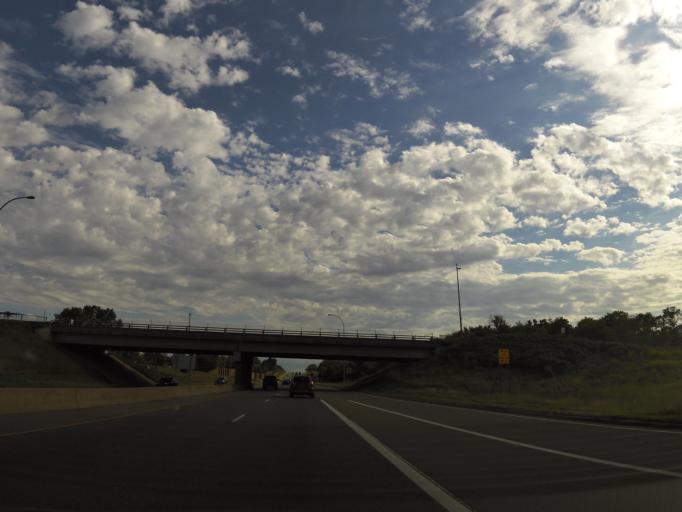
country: US
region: Minnesota
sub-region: Hennepin County
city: New Hope
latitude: 45.0083
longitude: -93.4011
